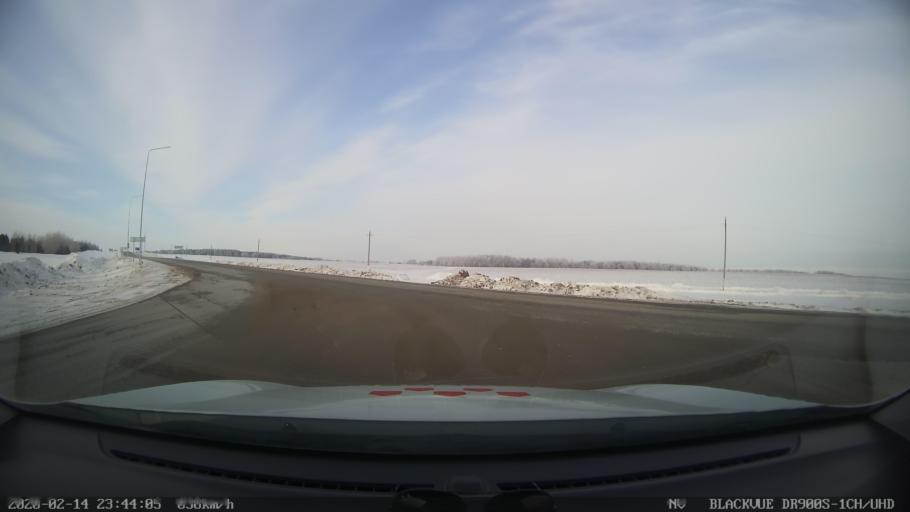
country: RU
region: Tatarstan
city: Kuybyshevskiy Zaton
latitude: 55.2089
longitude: 49.2471
